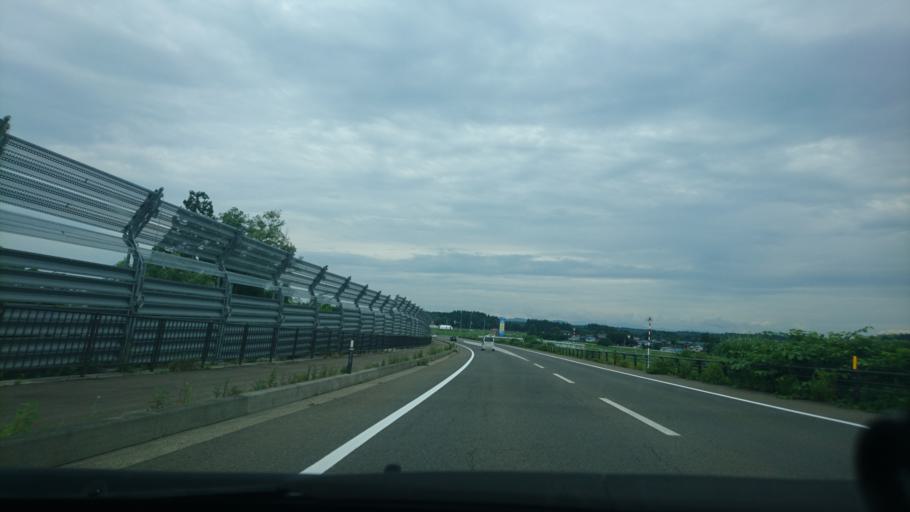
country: JP
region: Akita
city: Omagari
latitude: 39.4939
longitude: 140.4497
